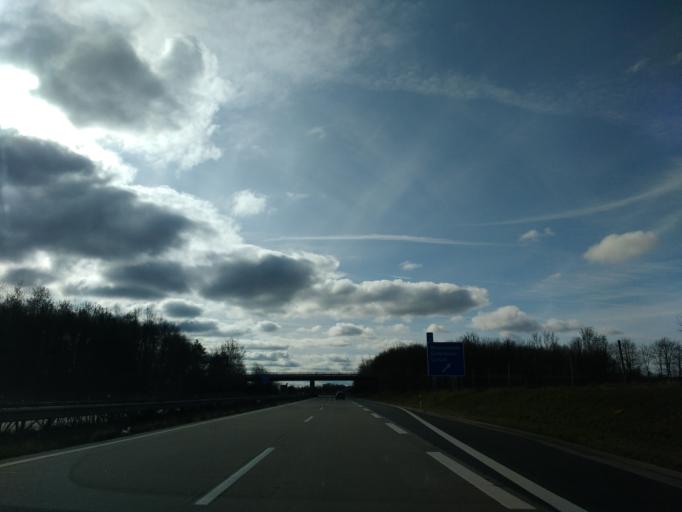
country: DE
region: Lower Saxony
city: Midlum
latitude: 53.6795
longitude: 8.6578
